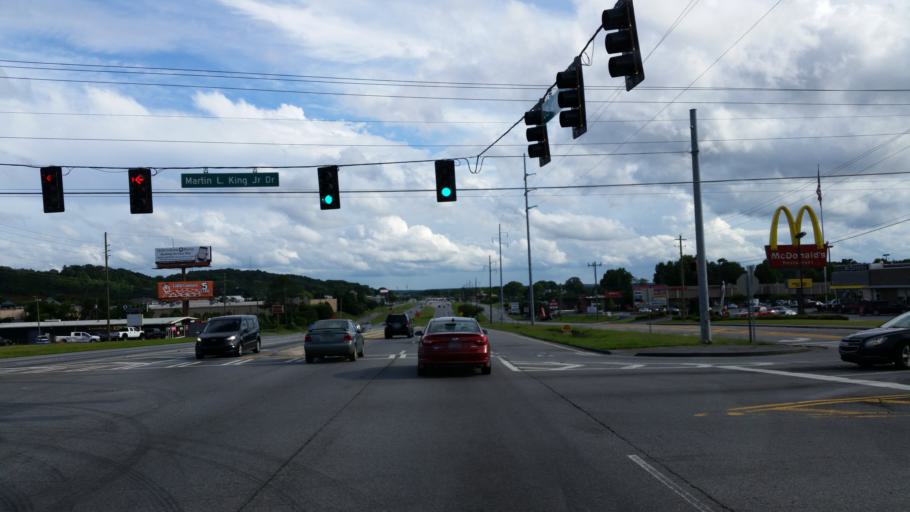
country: US
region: Georgia
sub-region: Bartow County
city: Cartersville
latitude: 34.1767
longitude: -84.7862
